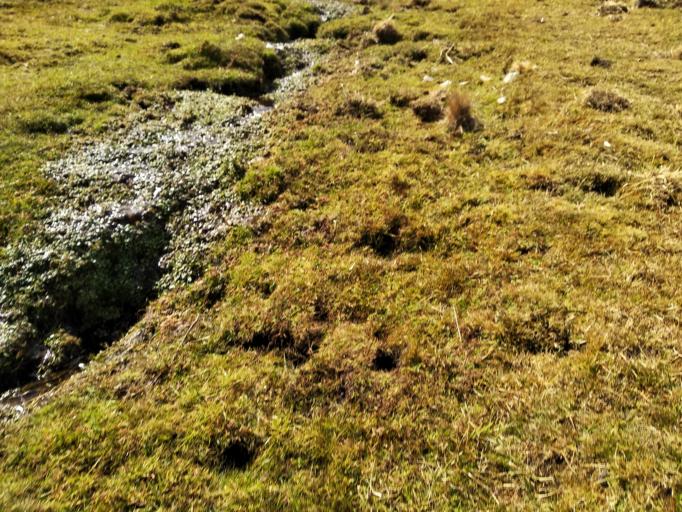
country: PE
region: Cusco
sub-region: Provincia de Urubamba
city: Ollantaytambo
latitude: -13.1256
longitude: -72.3360
